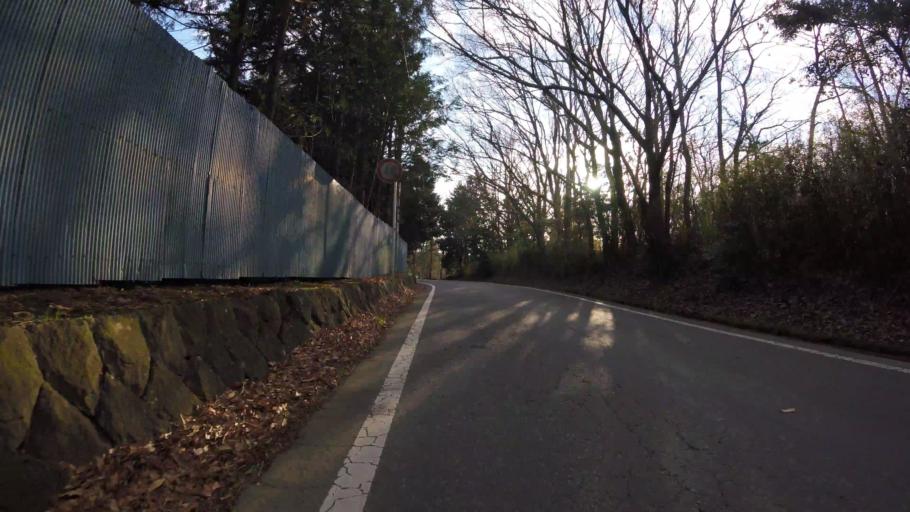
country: JP
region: Shizuoka
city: Mishima
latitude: 35.1068
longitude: 138.9804
